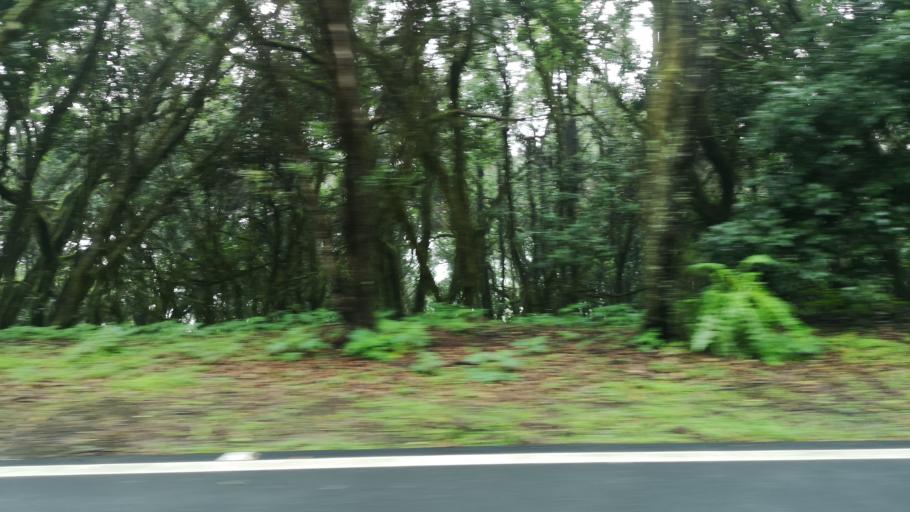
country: ES
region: Canary Islands
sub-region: Provincia de Santa Cruz de Tenerife
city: Vallehermosa
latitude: 28.1265
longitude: -17.2559
